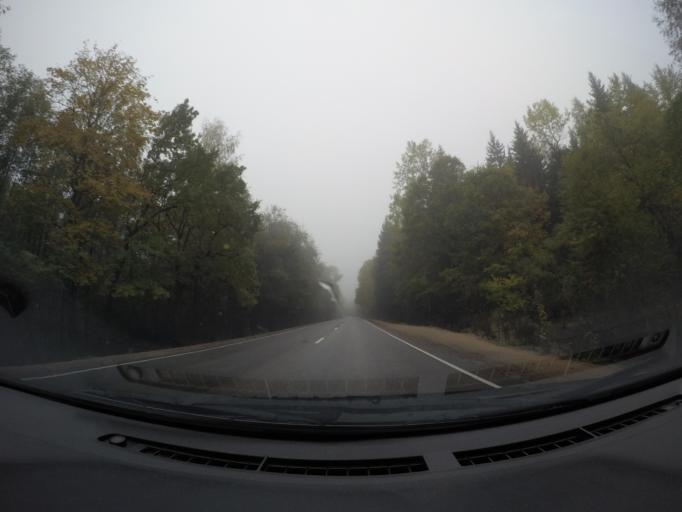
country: RU
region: Moskovskaya
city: Ruza
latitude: 55.7123
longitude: 36.2537
